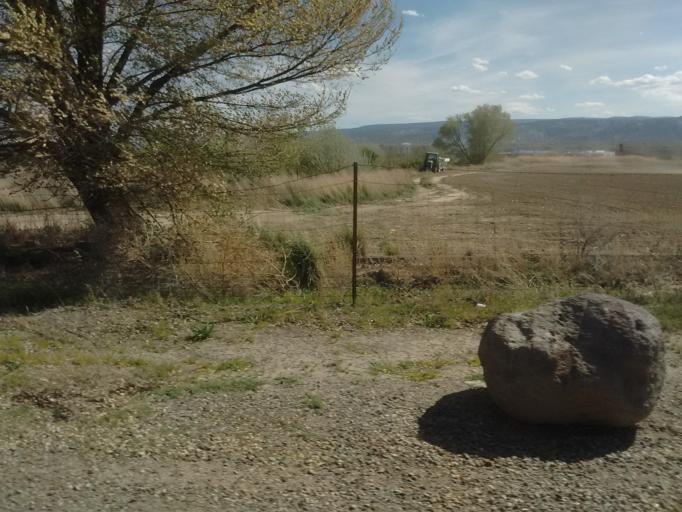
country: US
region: Colorado
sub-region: Mesa County
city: Redlands
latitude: 39.1063
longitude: -108.6042
